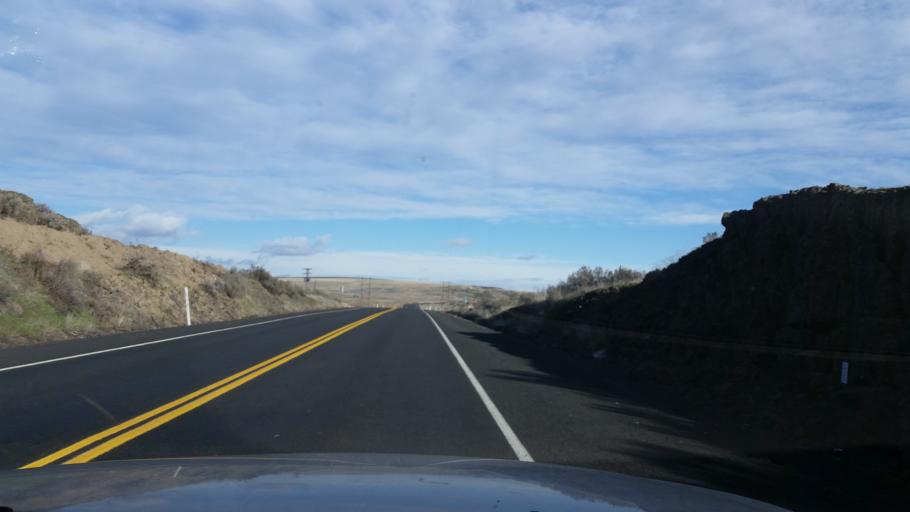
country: US
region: Washington
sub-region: Adams County
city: Ritzville
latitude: 47.3428
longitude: -118.6087
